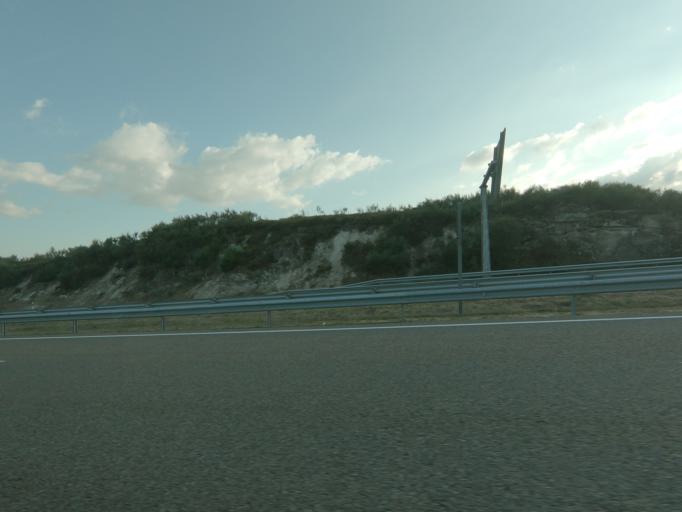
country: ES
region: Galicia
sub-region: Provincia de Ourense
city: Cualedro
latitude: 41.9857
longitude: -7.5488
